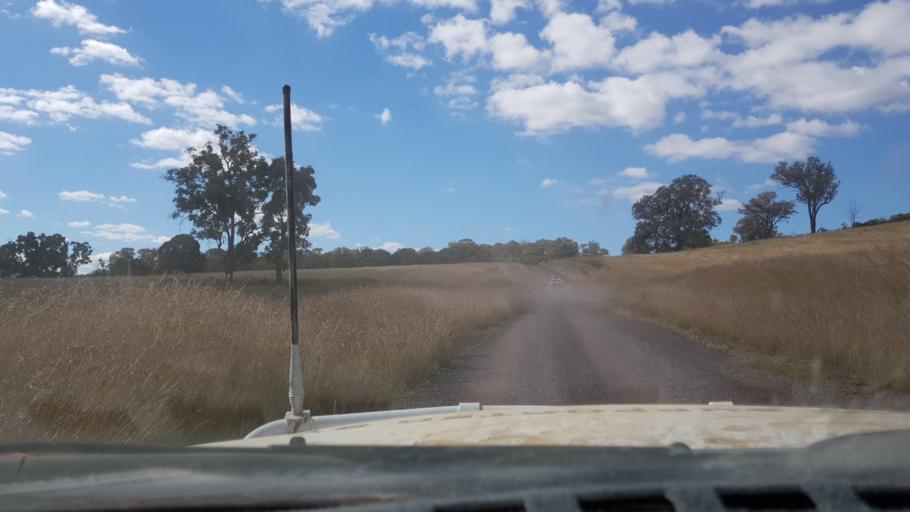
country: AU
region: New South Wales
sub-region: Tamworth Municipality
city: Manilla
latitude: -30.4271
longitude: 150.8113
